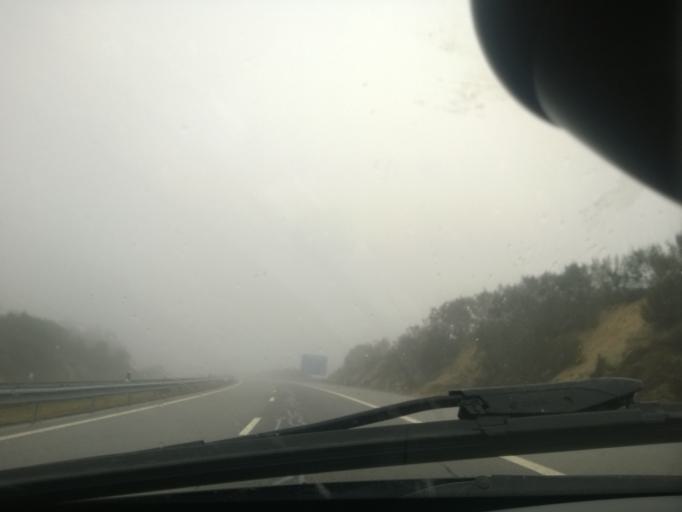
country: PT
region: Vila Real
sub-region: Vila Pouca de Aguiar
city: Vila Pouca de Aguiar
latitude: 41.5033
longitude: -7.7093
